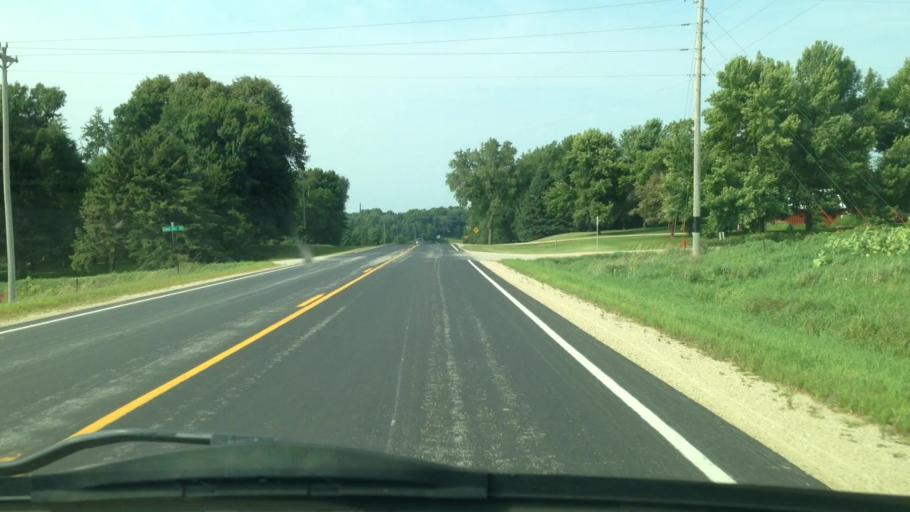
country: US
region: Minnesota
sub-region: Winona County
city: Lewiston
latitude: 43.9621
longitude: -91.9543
